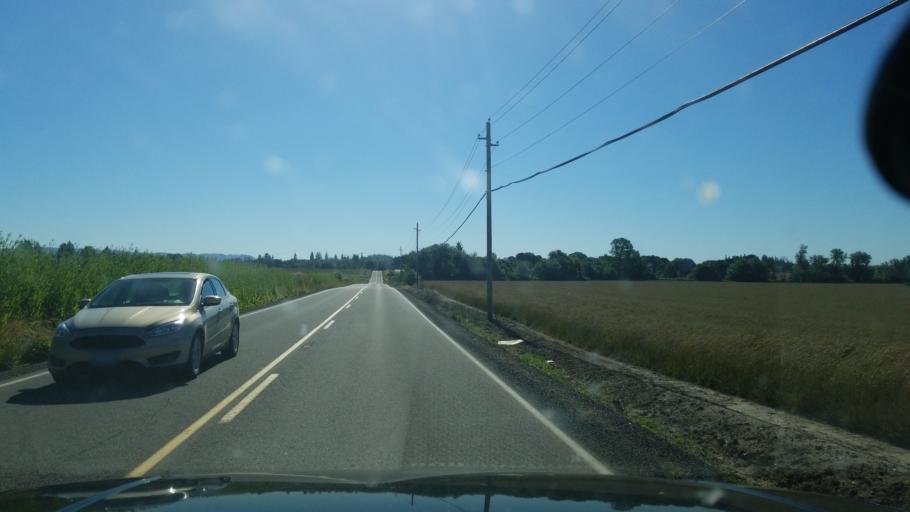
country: US
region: Oregon
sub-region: Yamhill County
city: McMinnville
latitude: 45.2305
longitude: -123.2423
